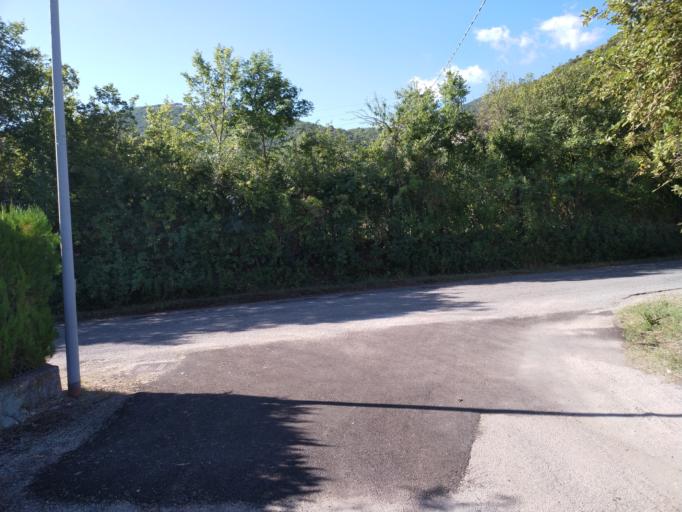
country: IT
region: Abruzzo
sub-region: Provincia dell' Aquila
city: Secinaro
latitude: 42.1798
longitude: 13.6651
